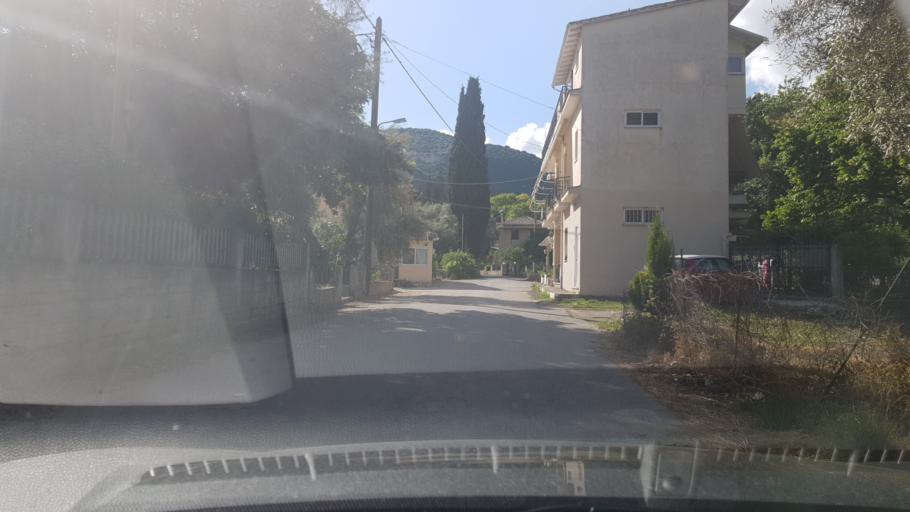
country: GR
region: Ionian Islands
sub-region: Lefkada
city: Nidri
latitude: 38.7146
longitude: 20.7014
